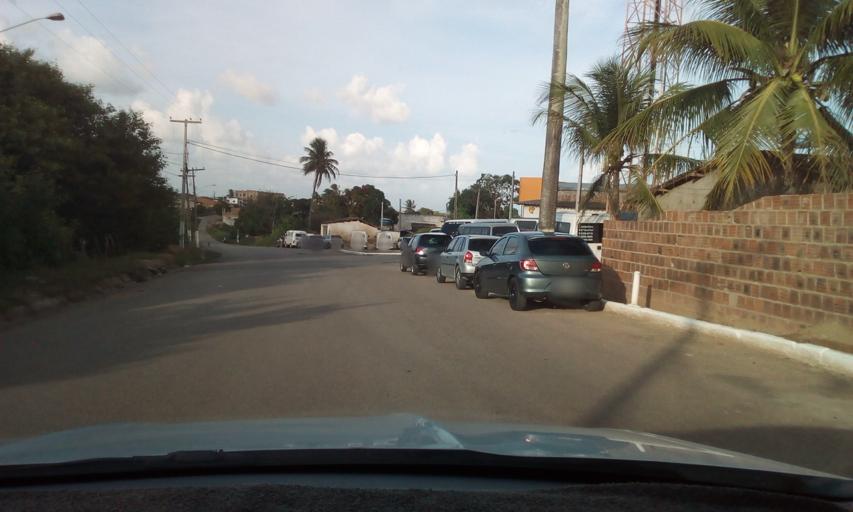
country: BR
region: Pernambuco
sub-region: Gloria Do Goita
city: Gloria do Goita
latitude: -7.9974
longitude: -35.2152
